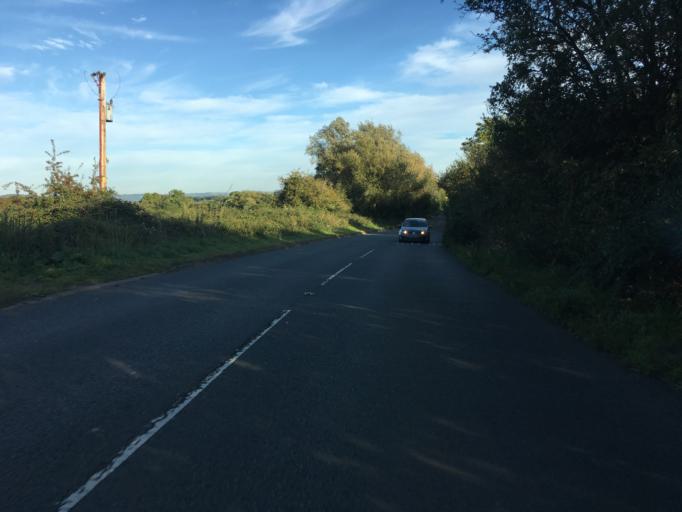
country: GB
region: England
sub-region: Worcestershire
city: Bredon
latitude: 52.0133
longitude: -2.1235
